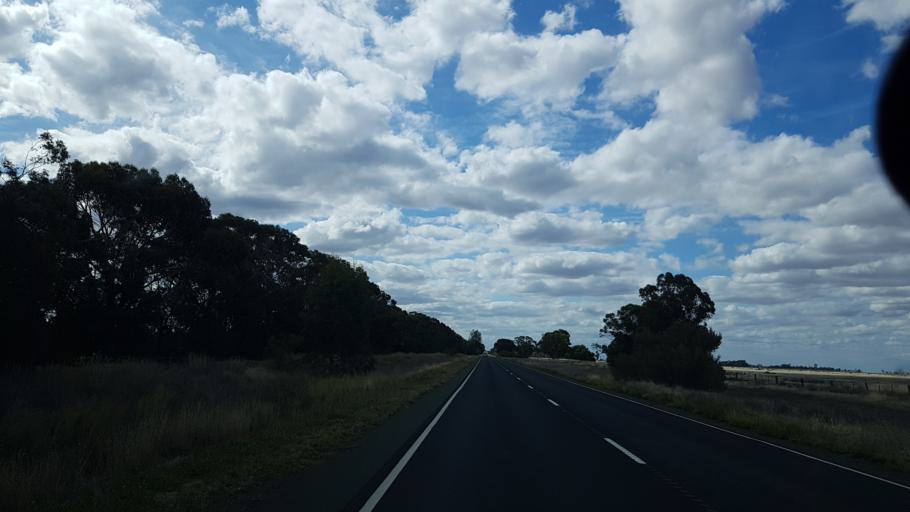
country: AU
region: Victoria
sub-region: Swan Hill
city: Swan Hill
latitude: -35.9854
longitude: 143.9455
